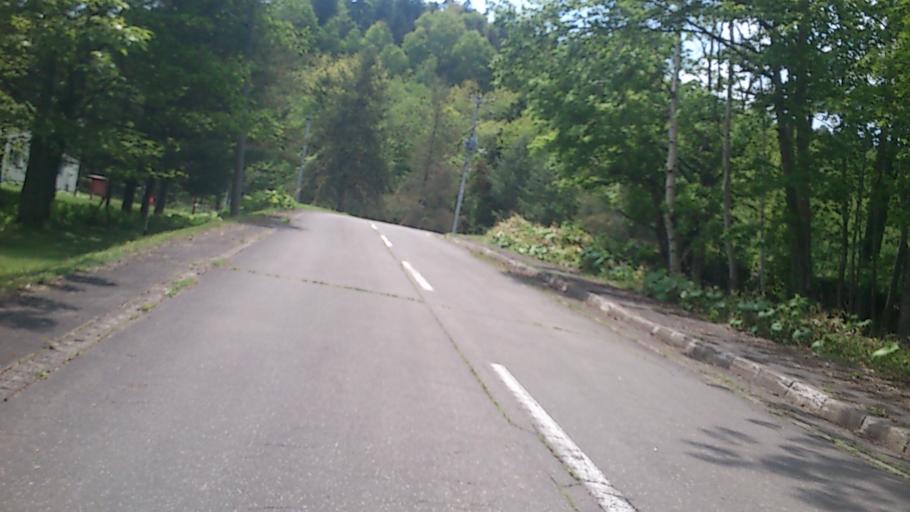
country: JP
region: Hokkaido
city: Otofuke
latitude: 43.3666
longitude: 143.1966
